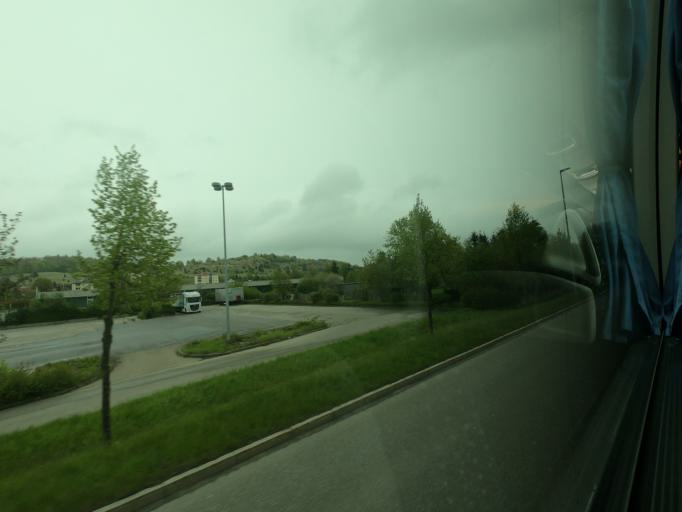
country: DE
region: Baden-Wuerttemberg
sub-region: Regierungsbezirk Stuttgart
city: Heidenheim an der Brenz
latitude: 48.7006
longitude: 10.1664
